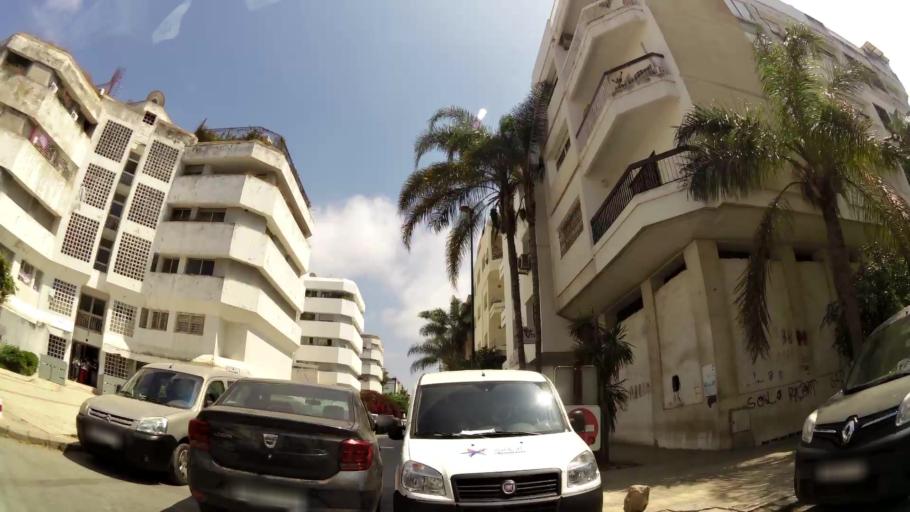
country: MA
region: Rabat-Sale-Zemmour-Zaer
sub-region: Rabat
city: Rabat
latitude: 33.9999
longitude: -6.8483
